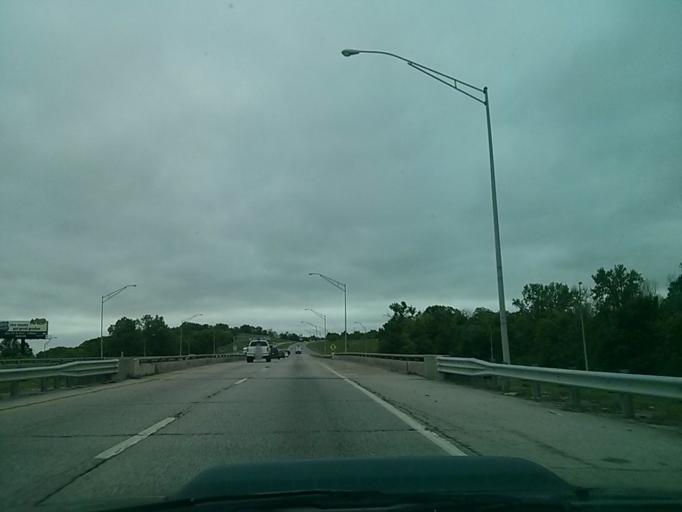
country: US
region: Oklahoma
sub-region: Tulsa County
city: Tulsa
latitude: 36.1050
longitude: -96.0098
